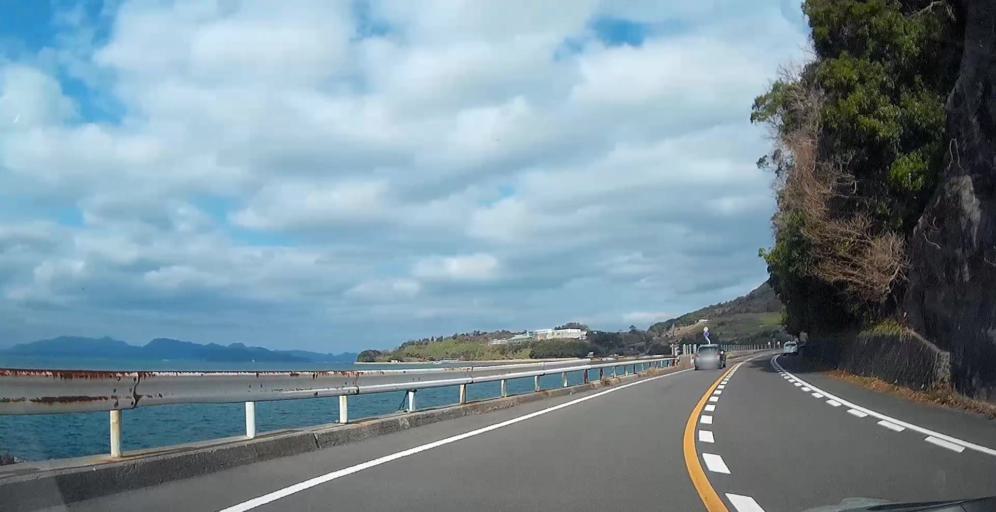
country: JP
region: Kumamoto
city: Minamata
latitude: 32.3121
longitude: 130.4693
